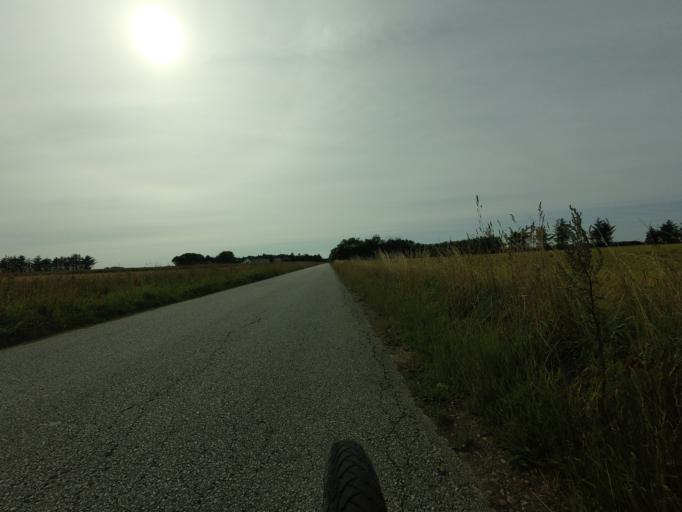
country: DK
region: North Denmark
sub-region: Hjorring Kommune
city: Hjorring
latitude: 57.4337
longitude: 9.8918
